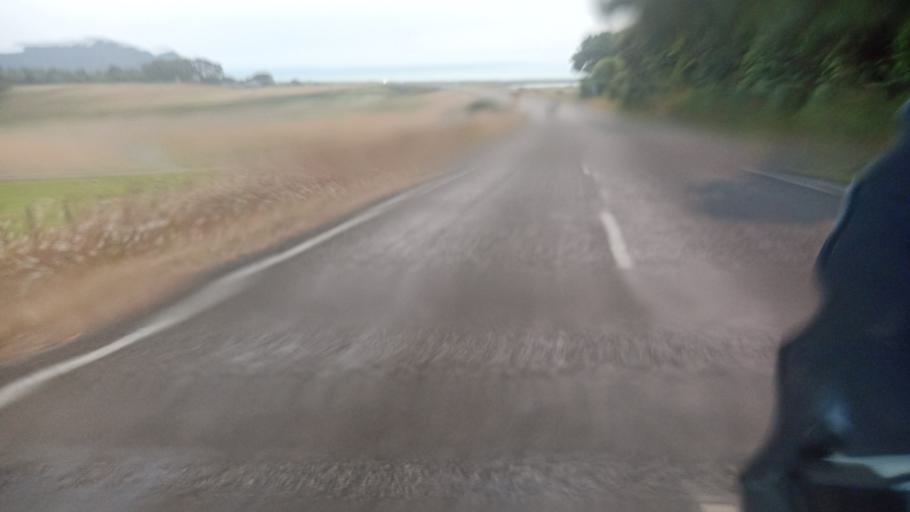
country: NZ
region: Bay of Plenty
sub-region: Opotiki District
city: Opotiki
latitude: -37.9200
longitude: 177.5359
